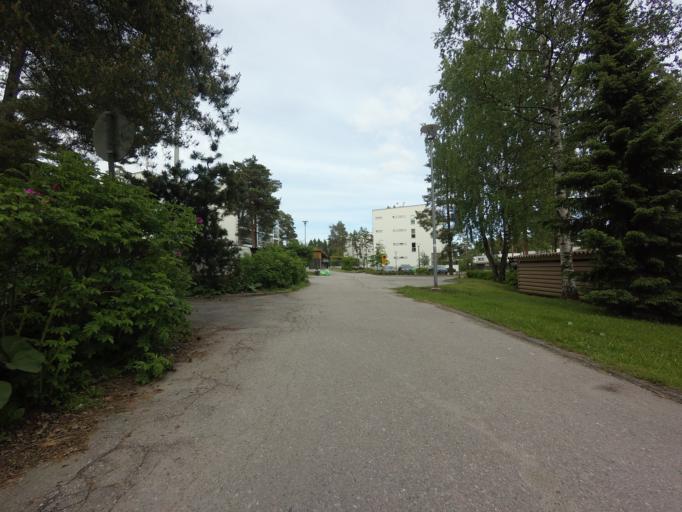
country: FI
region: Uusimaa
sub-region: Helsinki
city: Koukkuniemi
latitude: 60.1519
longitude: 24.7540
